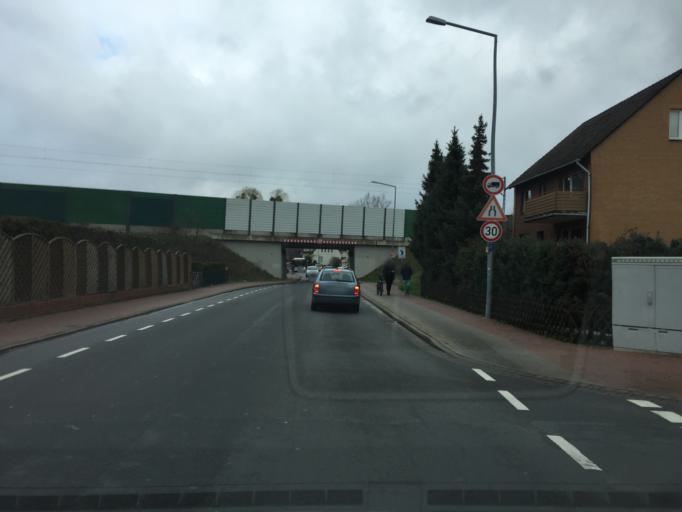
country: DE
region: Lower Saxony
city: Wunstorf
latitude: 52.4195
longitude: 9.4305
